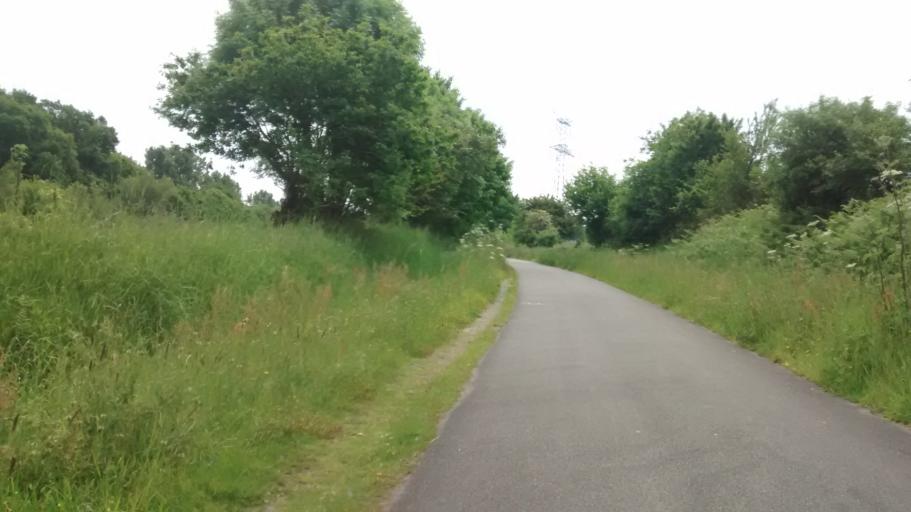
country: FR
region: Brittany
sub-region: Departement du Morbihan
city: Molac
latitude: 47.6998
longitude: -2.4354
